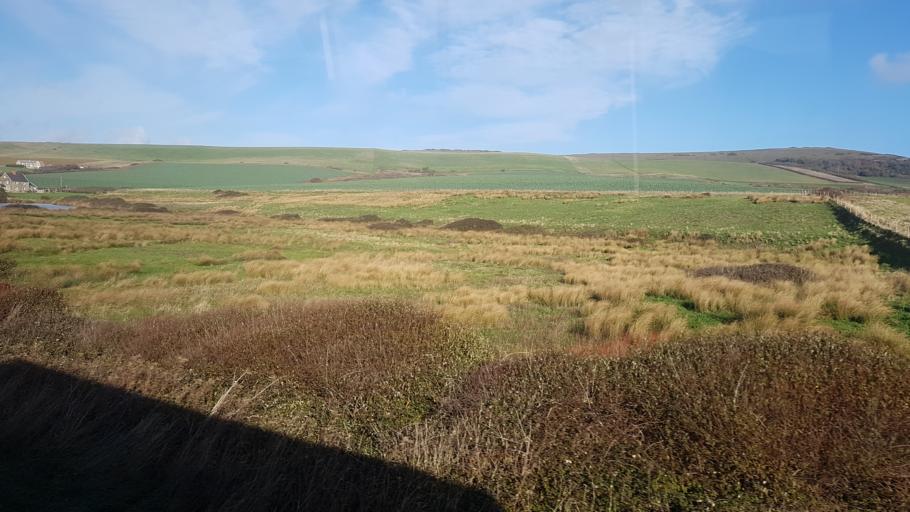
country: GB
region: England
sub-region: Isle of Wight
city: Freshwater
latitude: 50.6525
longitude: -1.4612
